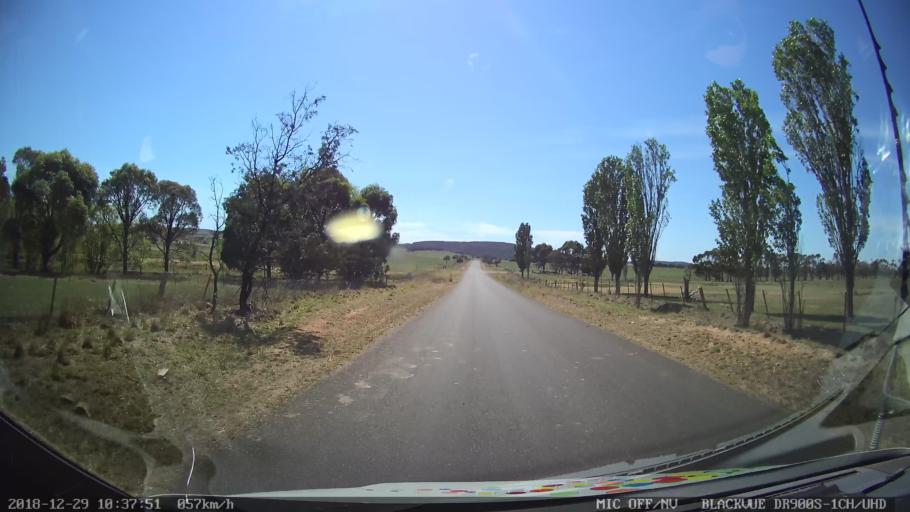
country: AU
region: New South Wales
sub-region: Yass Valley
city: Gundaroo
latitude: -34.9993
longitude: 149.5005
